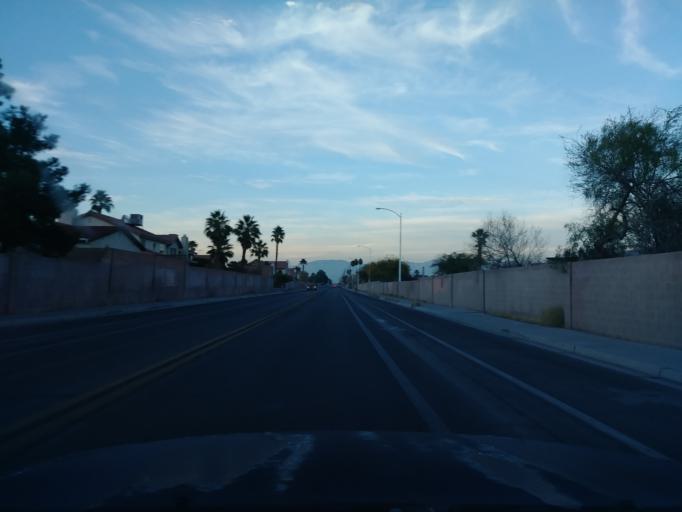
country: US
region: Nevada
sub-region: Clark County
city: Spring Valley
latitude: 36.1629
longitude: -115.2420
